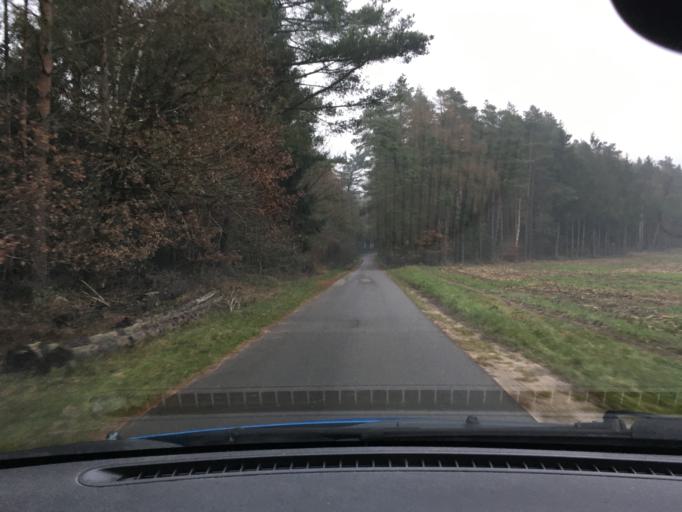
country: DE
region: Lower Saxony
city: Amelinghausen
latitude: 53.1022
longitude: 10.1855
